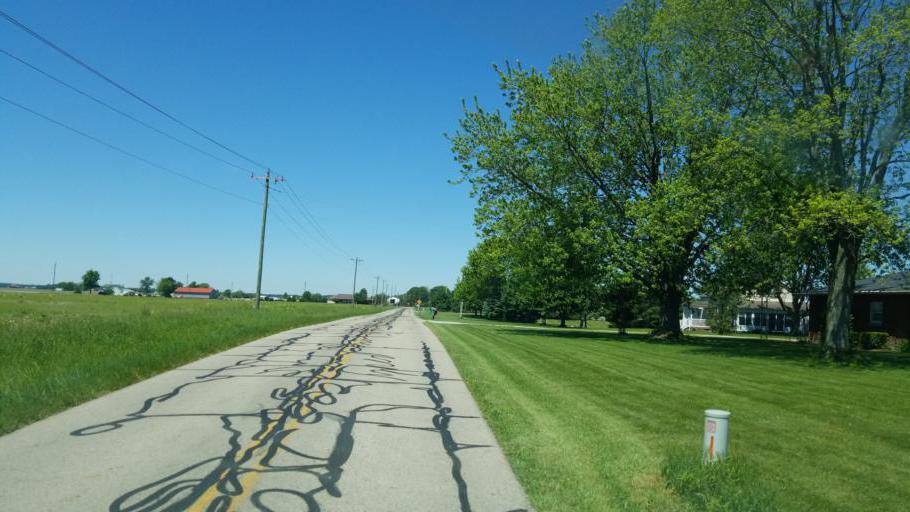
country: US
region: Ohio
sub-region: Shelby County
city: Anna
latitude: 40.3802
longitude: -84.2354
